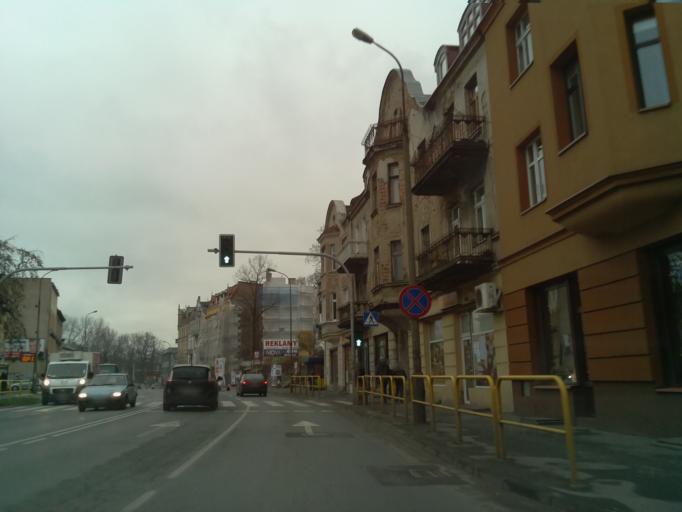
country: PL
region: Lower Silesian Voivodeship
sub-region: Jelenia Gora
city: Jelenia Gora
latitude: 50.8942
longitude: 15.7270
